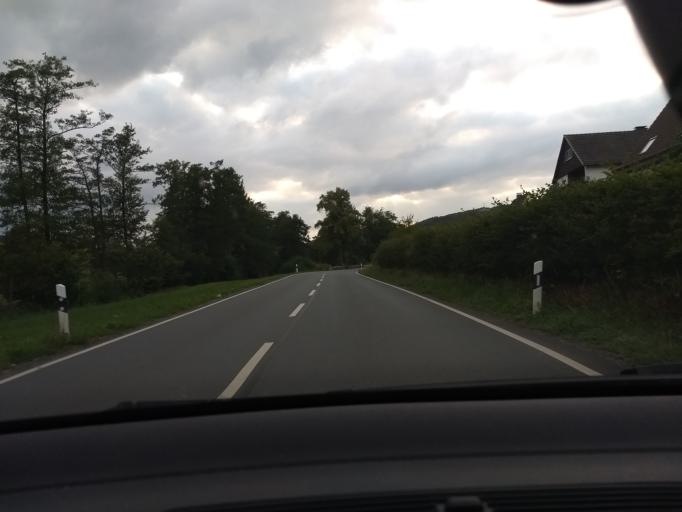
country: DE
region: North Rhine-Westphalia
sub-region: Regierungsbezirk Arnsberg
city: Arnsberg
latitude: 51.3559
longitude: 8.1606
